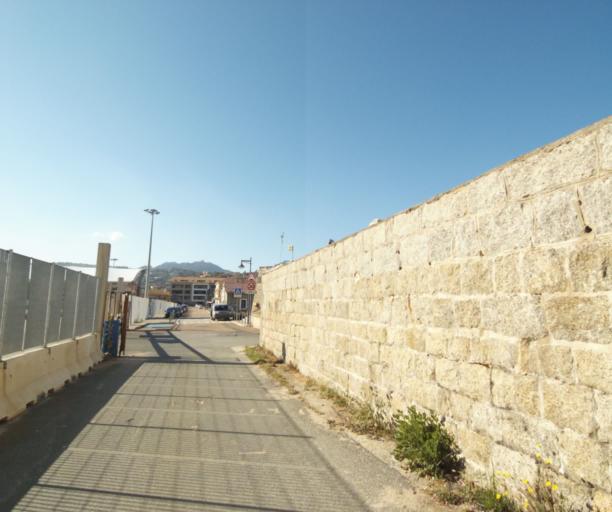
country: FR
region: Corsica
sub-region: Departement de la Corse-du-Sud
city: Propriano
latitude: 41.6774
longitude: 8.8977
